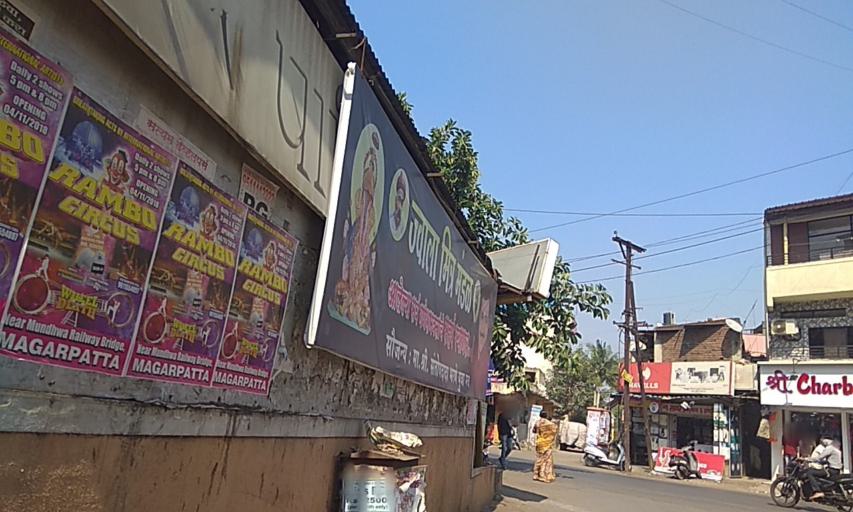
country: IN
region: Maharashtra
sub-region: Pune Division
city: Lohogaon
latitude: 18.5536
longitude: 73.9358
